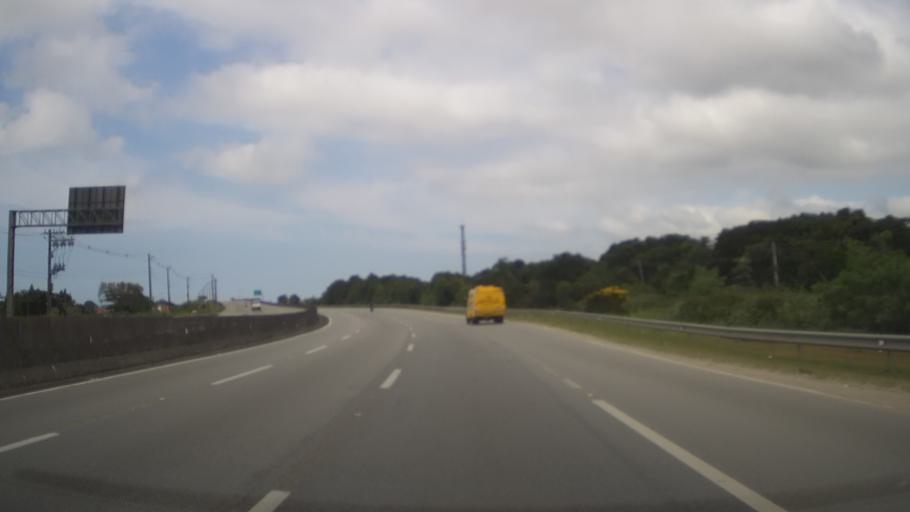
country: BR
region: Sao Paulo
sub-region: Praia Grande
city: Praia Grande
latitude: -23.9857
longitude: -46.4926
